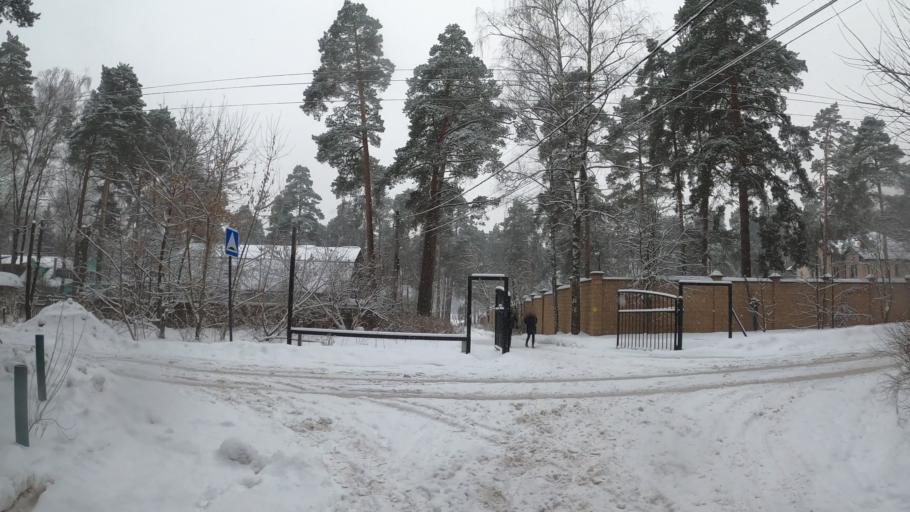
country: RU
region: Moskovskaya
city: Kratovo
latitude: 55.5887
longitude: 38.1622
